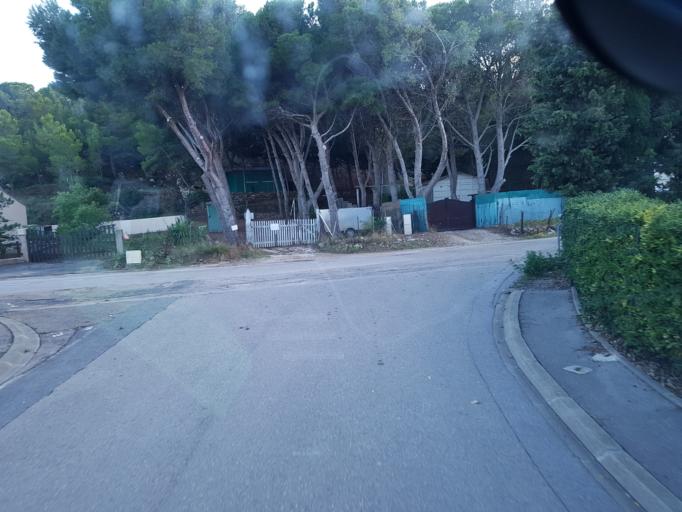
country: FR
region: Languedoc-Roussillon
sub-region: Departement de l'Aude
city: Leucate
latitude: 42.9348
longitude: 3.0265
